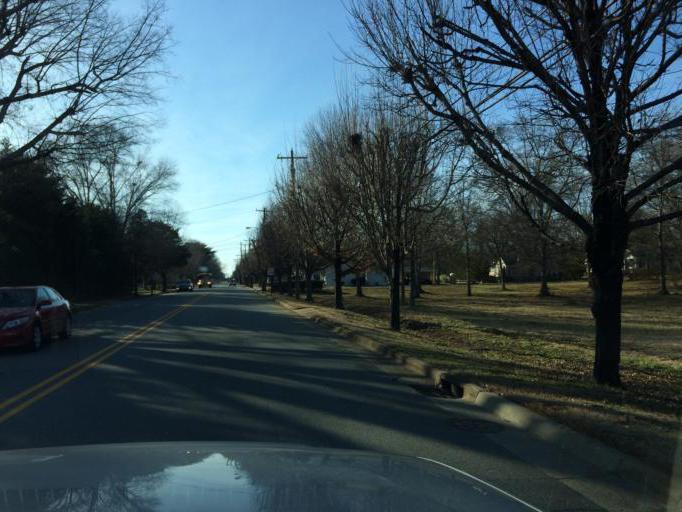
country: US
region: North Carolina
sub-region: Rutherford County
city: Forest City
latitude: 35.3321
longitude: -81.8518
